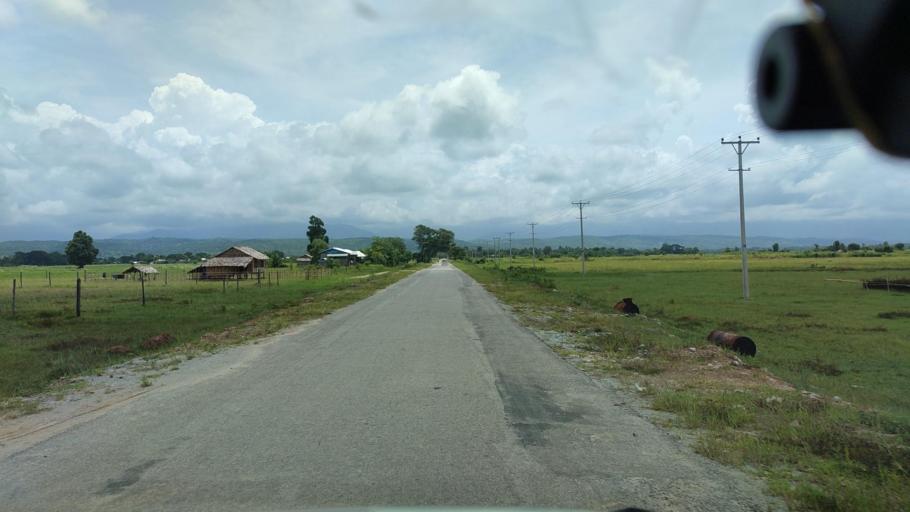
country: MM
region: Bago
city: Taungoo
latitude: 19.1499
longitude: 96.4038
